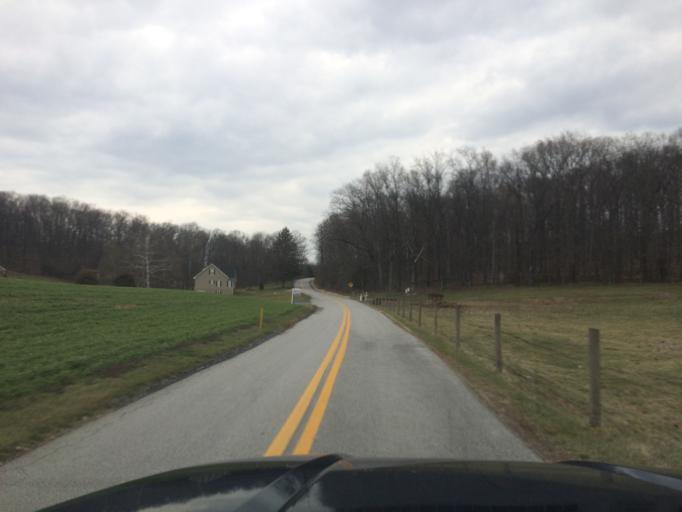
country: US
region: Maryland
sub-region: Carroll County
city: New Windsor
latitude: 39.5334
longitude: -77.1460
